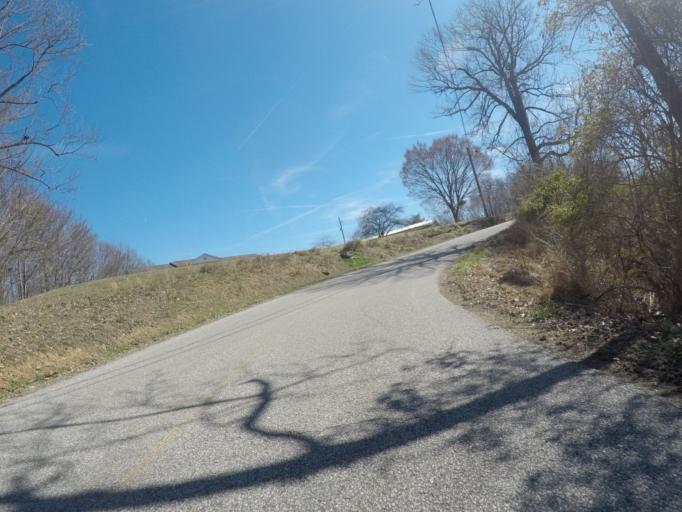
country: US
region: West Virginia
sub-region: Cabell County
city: Huntington
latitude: 38.4504
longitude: -82.4880
